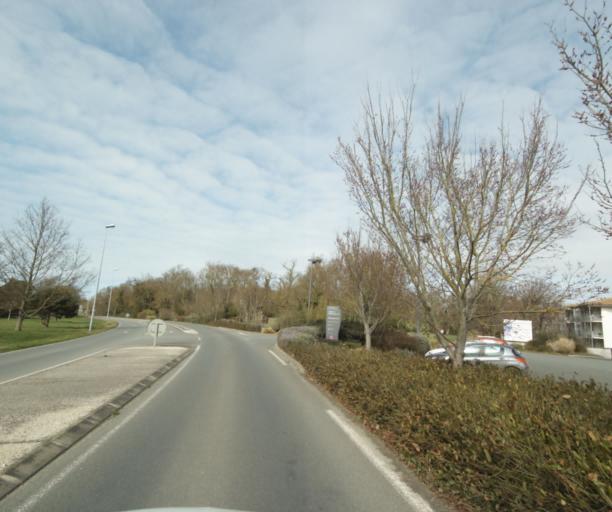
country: FR
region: Poitou-Charentes
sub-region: Departement de la Charente-Maritime
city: Lagord
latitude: 46.1843
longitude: -1.1746
